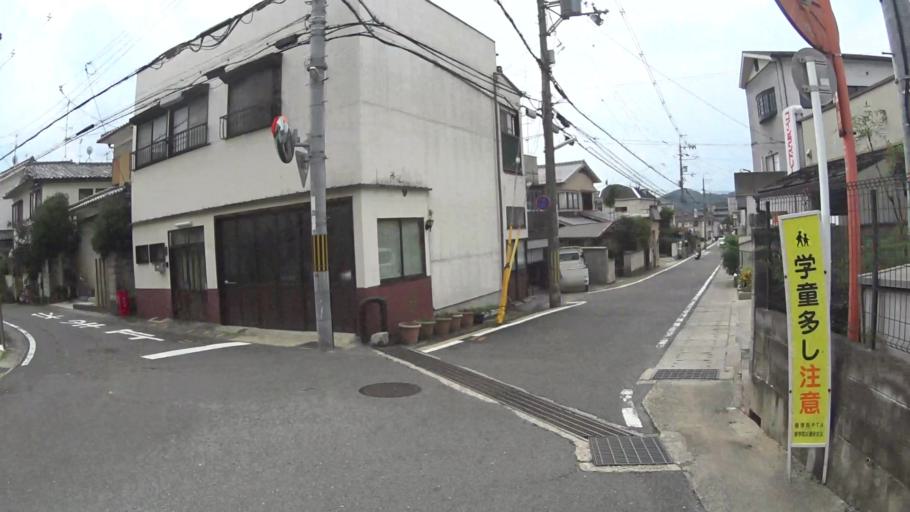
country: JP
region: Kyoto
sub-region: Kyoto-shi
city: Kamigyo-ku
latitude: 35.0514
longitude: 135.7958
